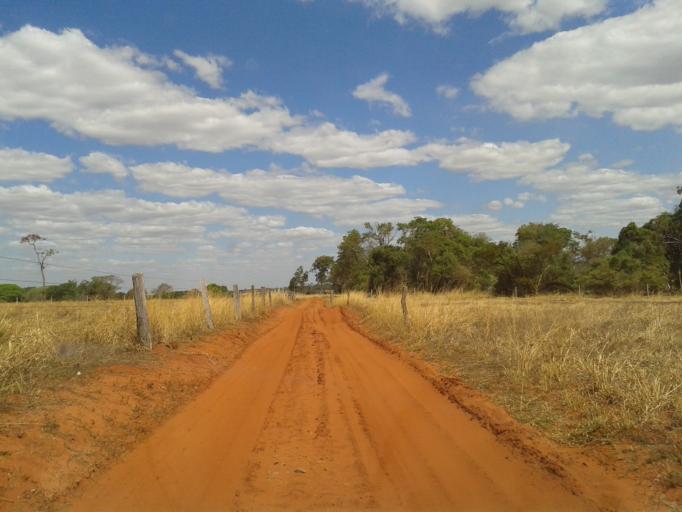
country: BR
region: Minas Gerais
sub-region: Centralina
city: Centralina
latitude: -18.7738
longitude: -49.0899
